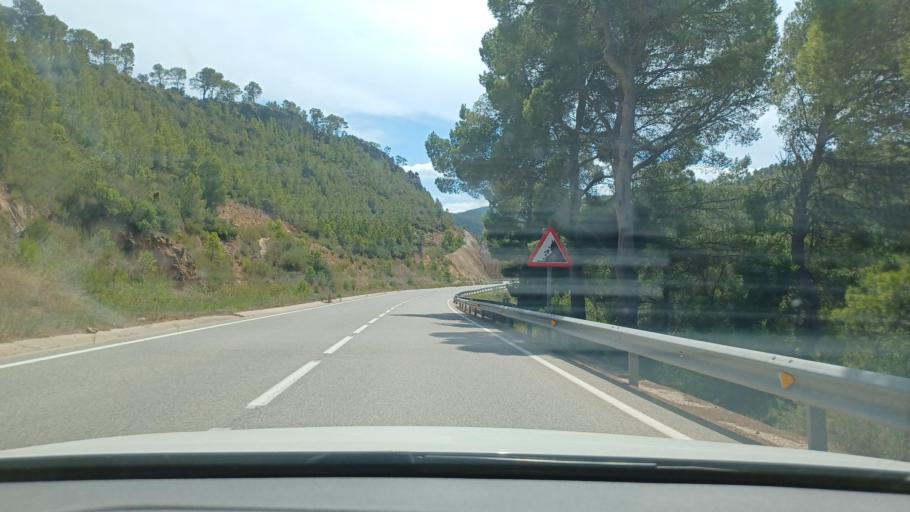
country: ES
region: Catalonia
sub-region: Provincia de Tarragona
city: Benifallet
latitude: 40.9682
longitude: 0.4459
